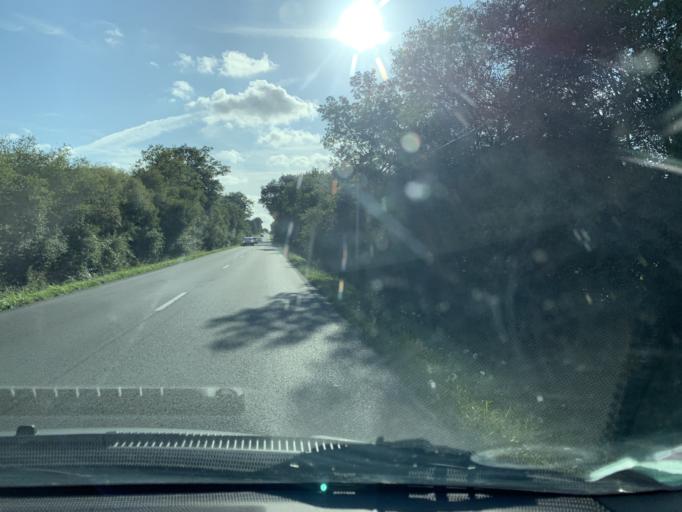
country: FR
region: Brittany
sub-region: Departement du Morbihan
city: Ambon
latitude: 47.5559
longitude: -2.5268
